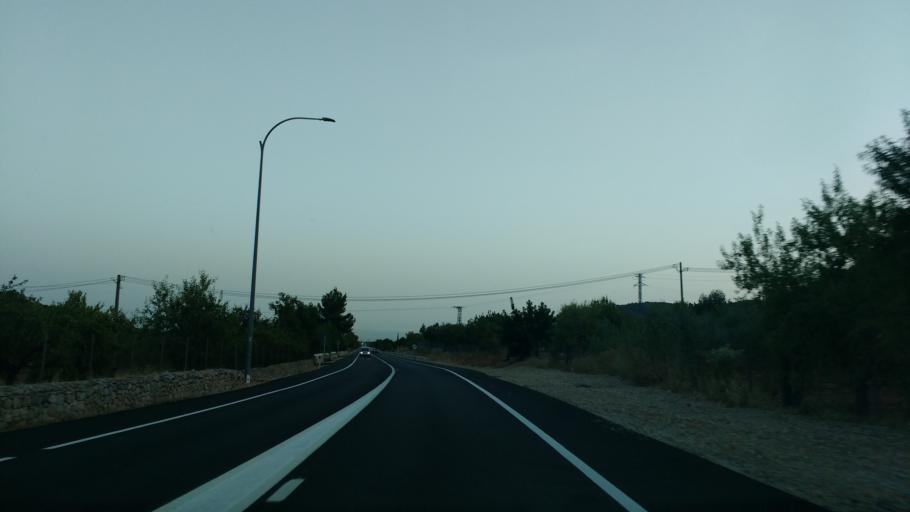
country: ES
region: Balearic Islands
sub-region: Illes Balears
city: Bunyola
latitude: 39.6944
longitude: 2.6864
